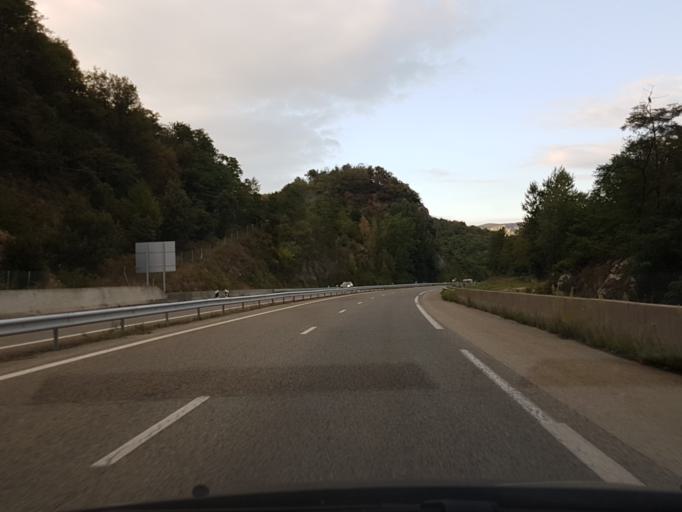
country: FR
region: Midi-Pyrenees
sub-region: Departement de l'Ariege
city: Mercus-Garrabet
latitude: 42.8943
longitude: 1.6300
